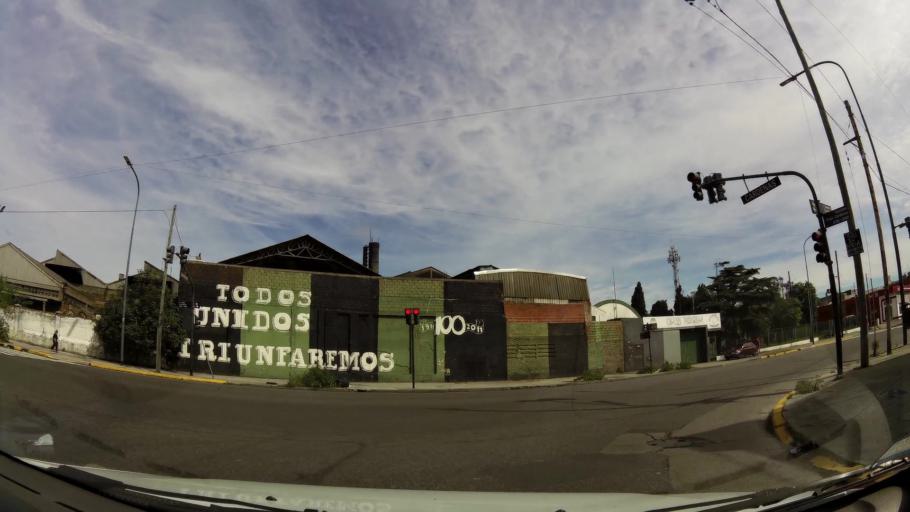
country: AR
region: Buenos Aires F.D.
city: Villa Lugano
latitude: -34.6725
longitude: -58.4990
